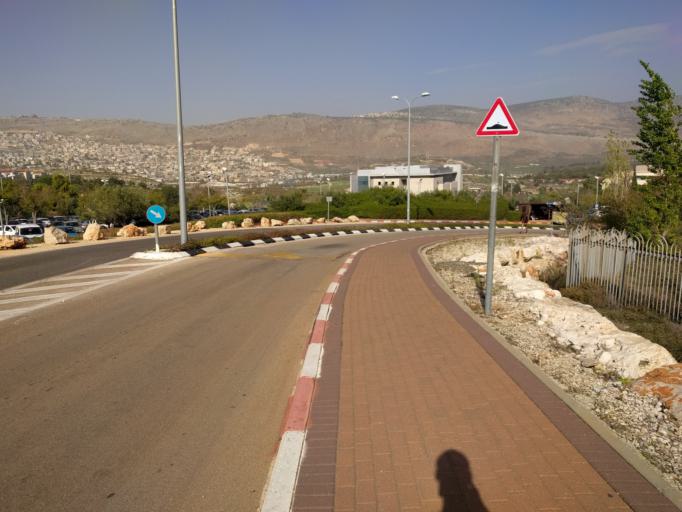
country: IL
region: Northern District
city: Karmi'el
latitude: 32.9125
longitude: 35.2806
